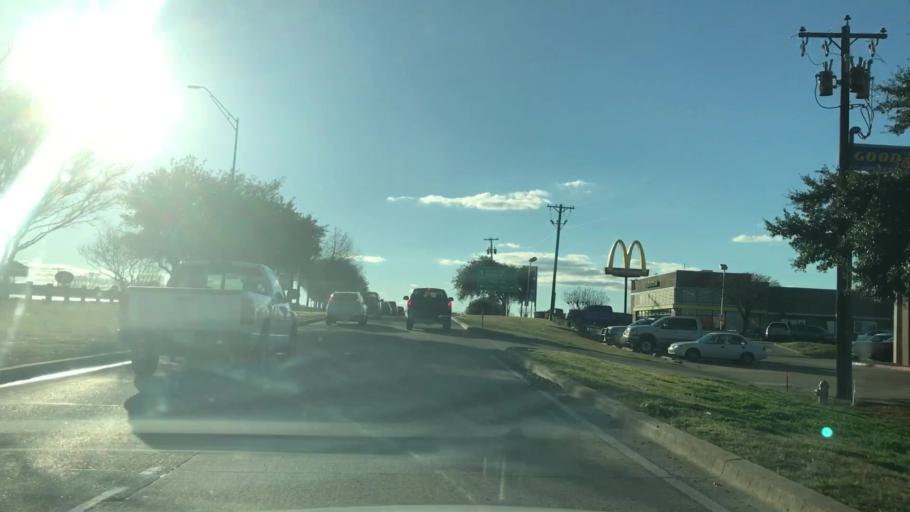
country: US
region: Texas
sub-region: Rockwall County
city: Rockwall
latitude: 32.8993
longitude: -96.4684
